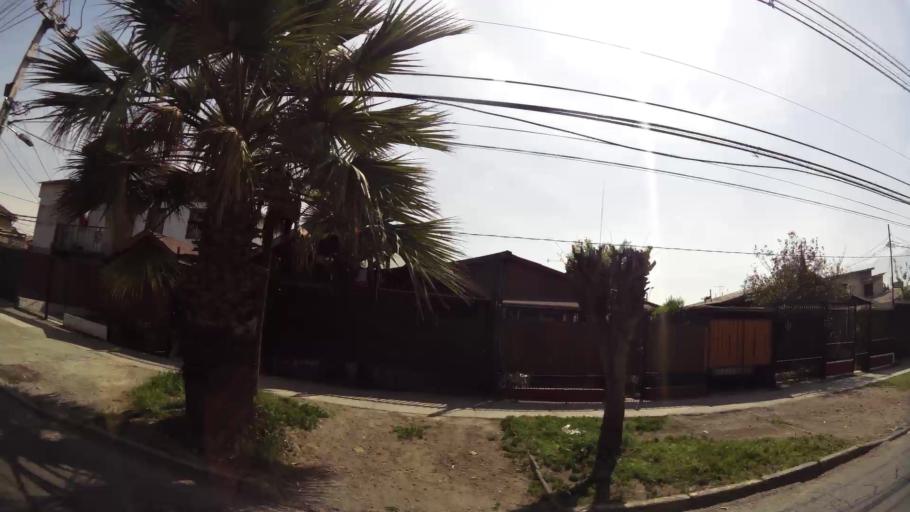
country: CL
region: Santiago Metropolitan
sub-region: Provincia de Santiago
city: Villa Presidente Frei, Nunoa, Santiago, Chile
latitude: -33.5059
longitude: -70.5820
